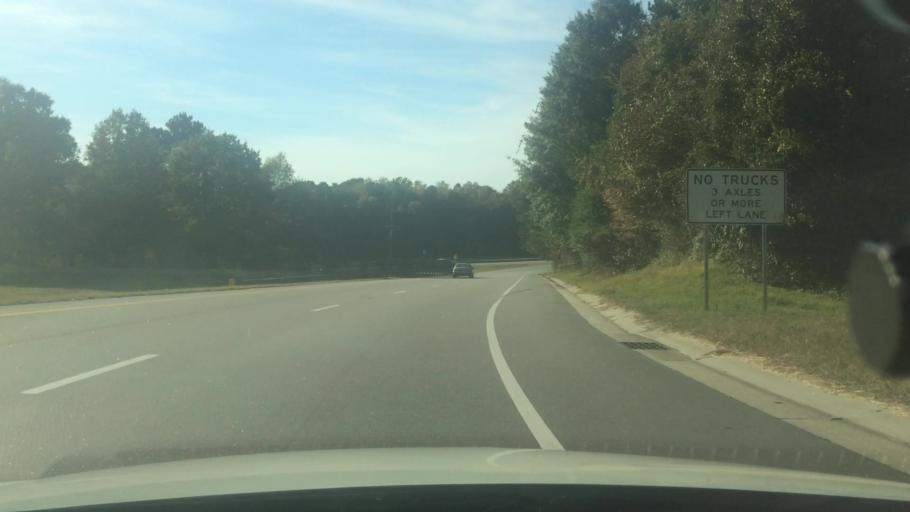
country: US
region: North Carolina
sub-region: Wake County
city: Raleigh
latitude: 35.8158
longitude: -78.6037
